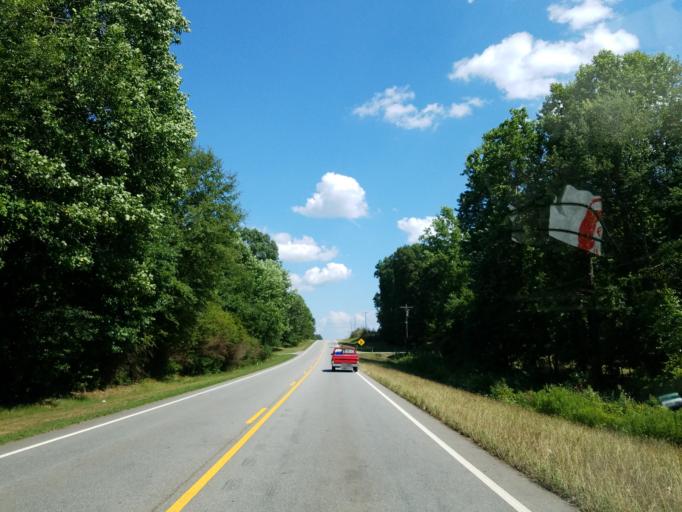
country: US
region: Georgia
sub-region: Lamar County
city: Barnesville
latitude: 33.0202
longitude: -84.1349
